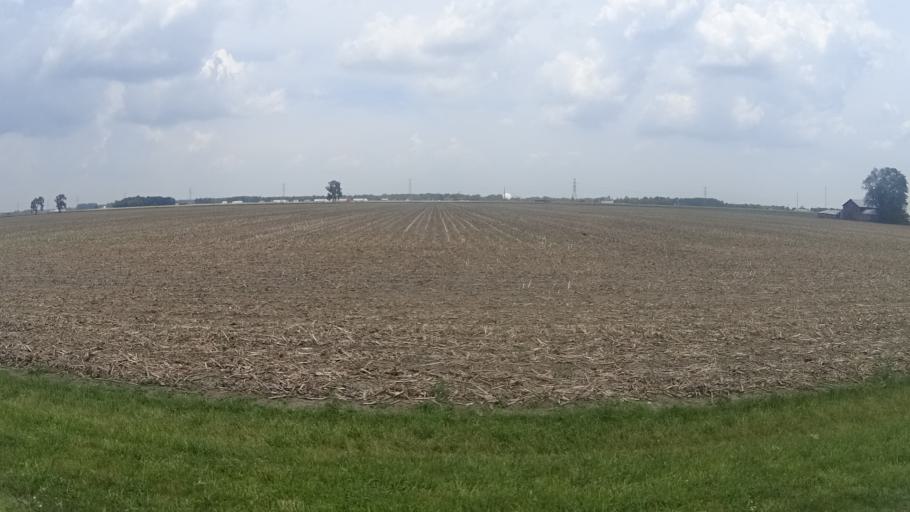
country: US
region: Ohio
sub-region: Erie County
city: Milan
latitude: 41.3228
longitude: -82.6539
